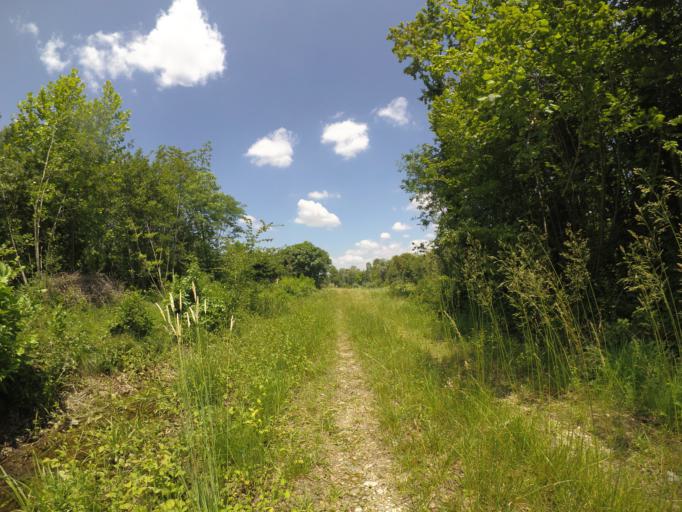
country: IT
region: Friuli Venezia Giulia
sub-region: Provincia di Udine
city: Bertiolo
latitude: 45.9311
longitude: 13.0748
